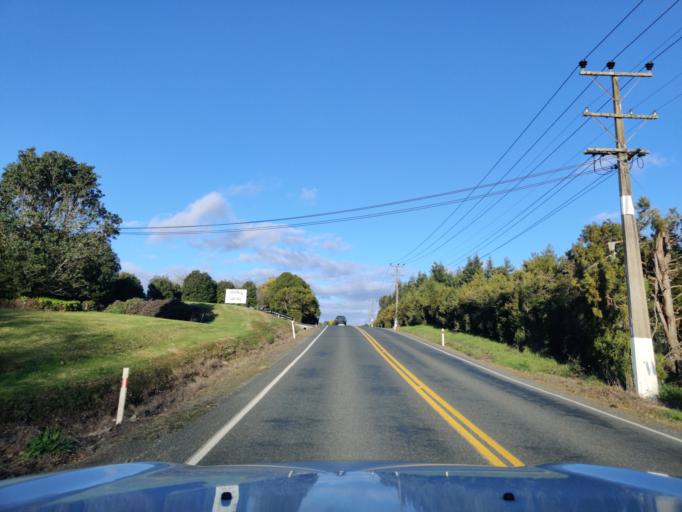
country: NZ
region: Auckland
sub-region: Auckland
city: Pakuranga
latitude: -36.9606
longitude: 174.9753
